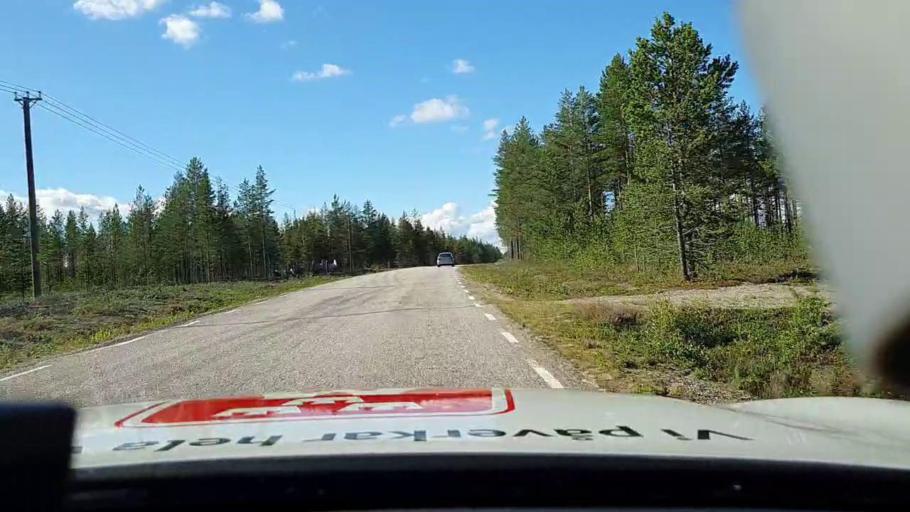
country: SE
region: Norrbotten
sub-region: Overkalix Kommun
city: OEverkalix
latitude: 66.2377
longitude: 22.9327
